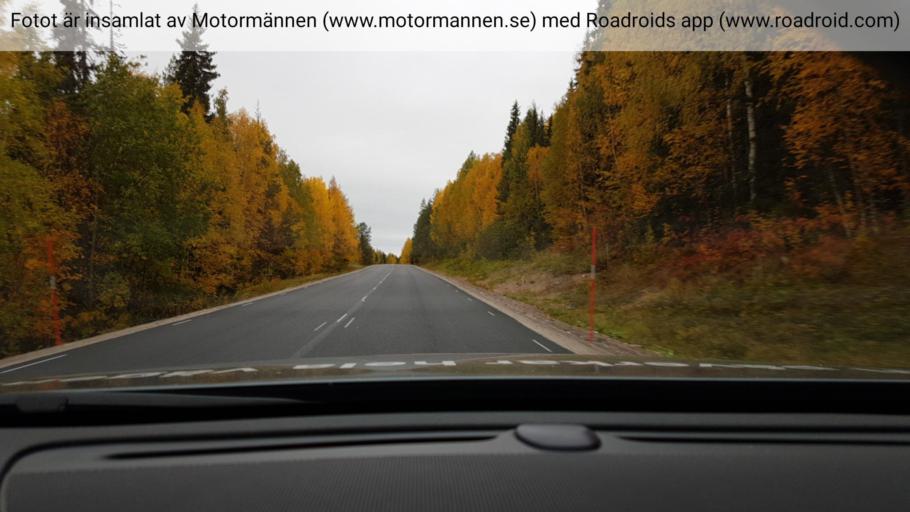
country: SE
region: Norrbotten
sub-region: Overkalix Kommun
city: OEverkalix
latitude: 66.4849
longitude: 22.7834
